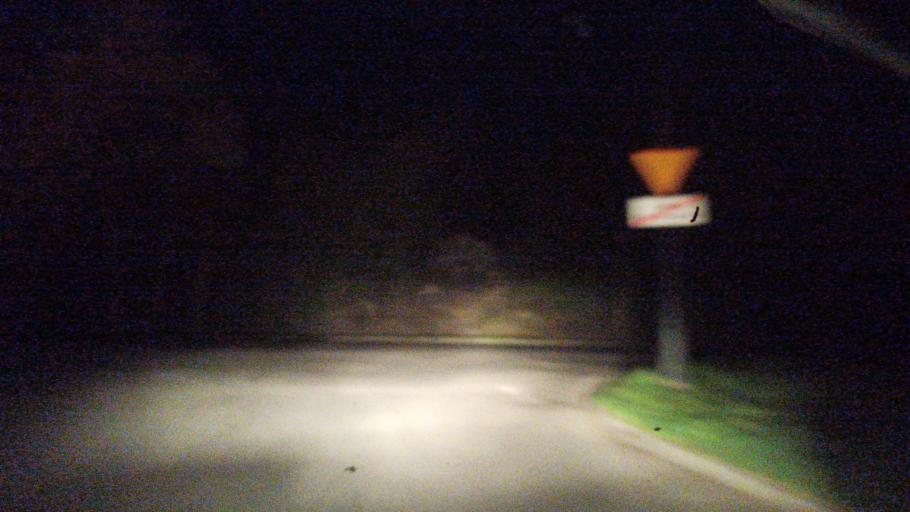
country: PL
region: Warmian-Masurian Voivodeship
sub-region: Powiat elblaski
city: Gronowo Gorne
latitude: 54.1613
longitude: 19.4608
